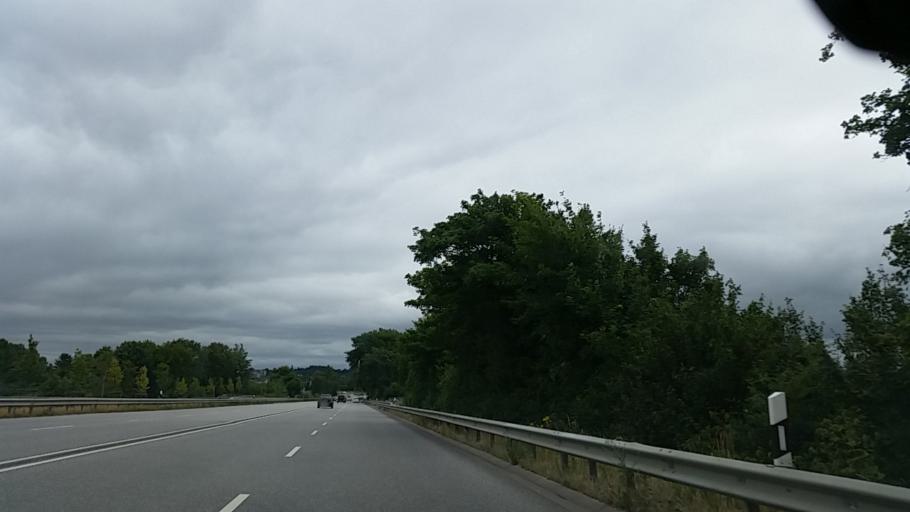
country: DE
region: Schleswig-Holstein
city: Windeby
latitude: 54.4768
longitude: 9.8224
